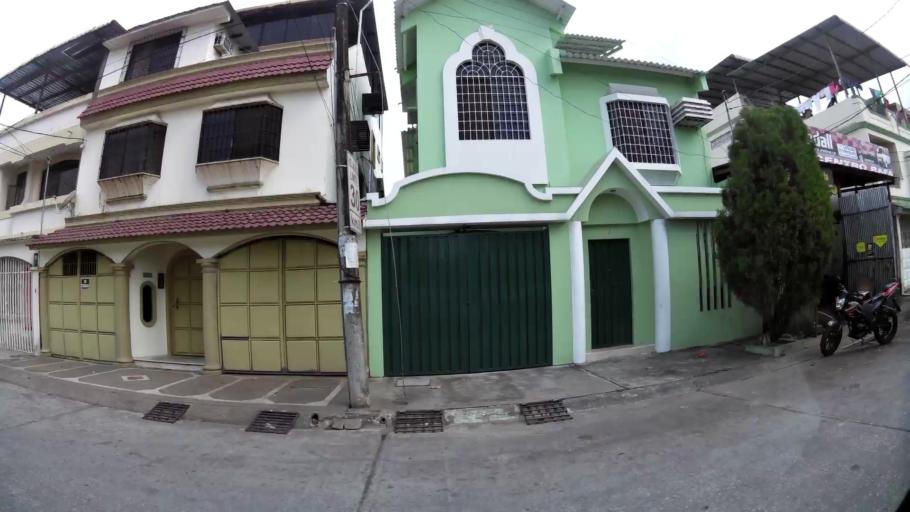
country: EC
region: Guayas
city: Eloy Alfaro
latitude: -2.1169
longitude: -79.8895
